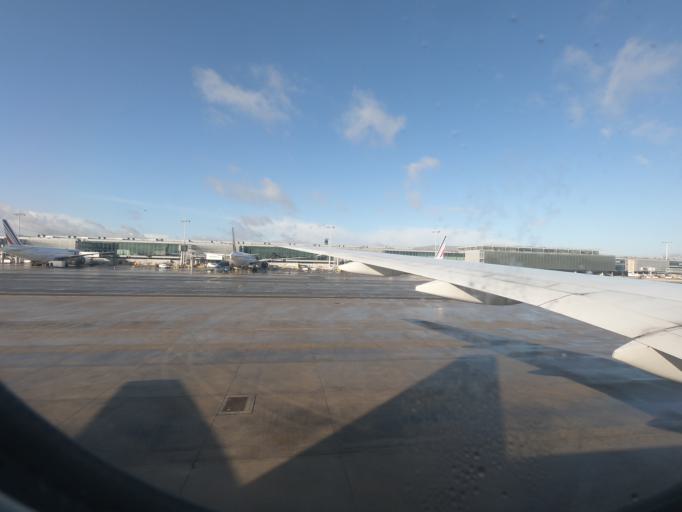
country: FR
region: Ile-de-France
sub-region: Departement de Seine-et-Marne
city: Mitry-Mory
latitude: 49.0032
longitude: 2.5886
